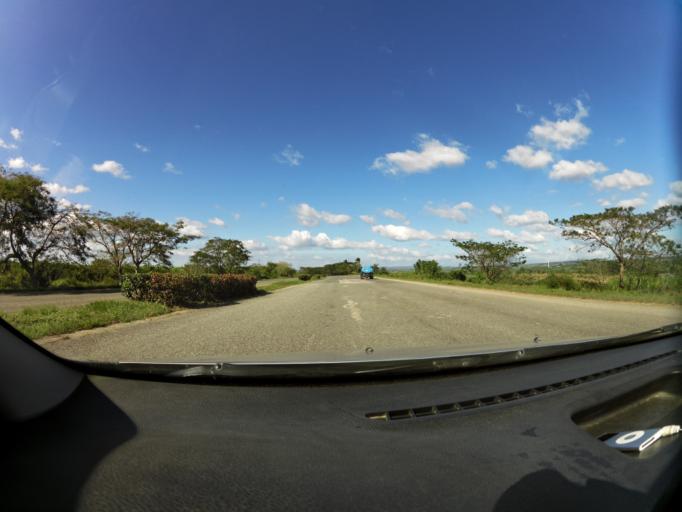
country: CU
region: Santiago de Cuba
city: San Luis
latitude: 20.1239
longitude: -75.7589
